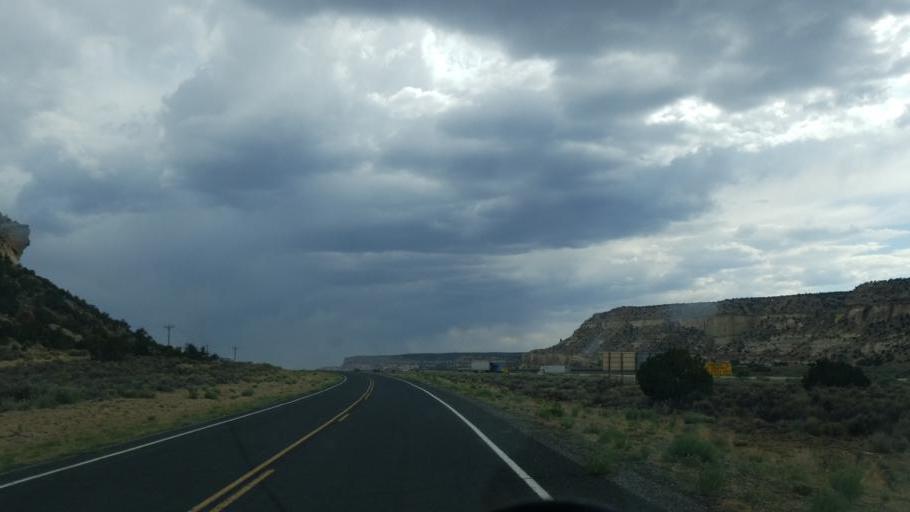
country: US
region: Arizona
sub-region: Apache County
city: Houck
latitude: 35.4104
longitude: -108.9964
